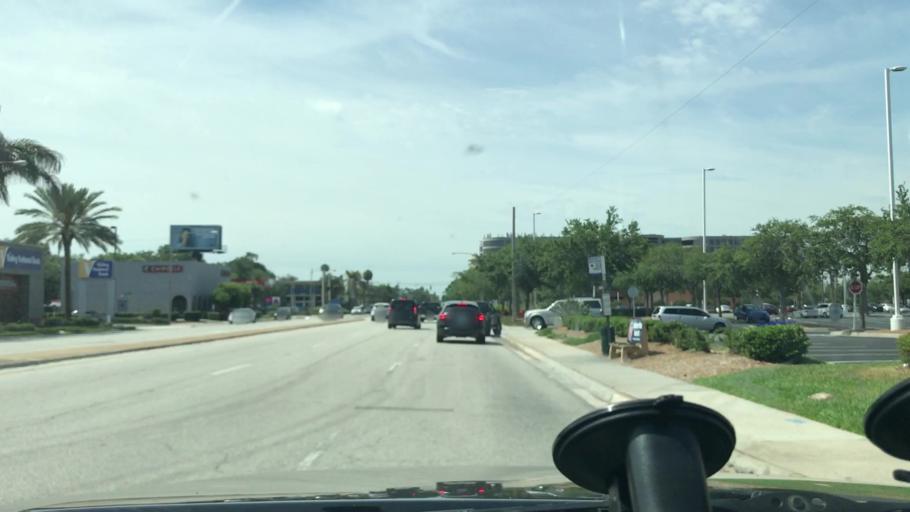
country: US
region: Florida
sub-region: Hillsborough County
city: Tampa
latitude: 27.9485
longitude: -82.5243
